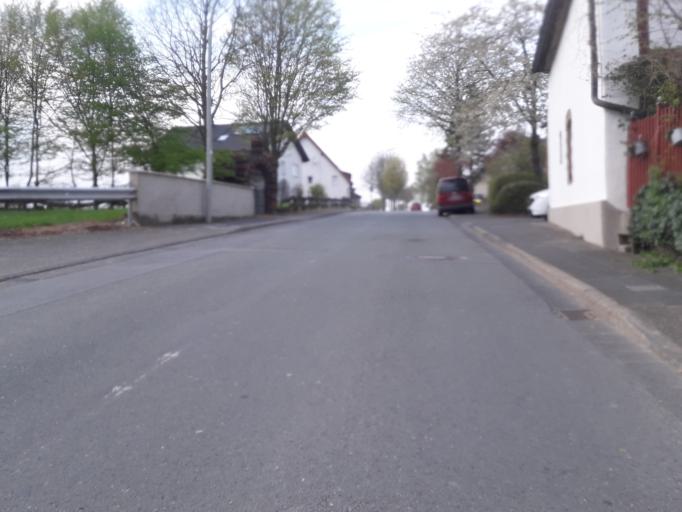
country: DE
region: North Rhine-Westphalia
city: Lichtenau
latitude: 51.6742
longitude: 8.8325
